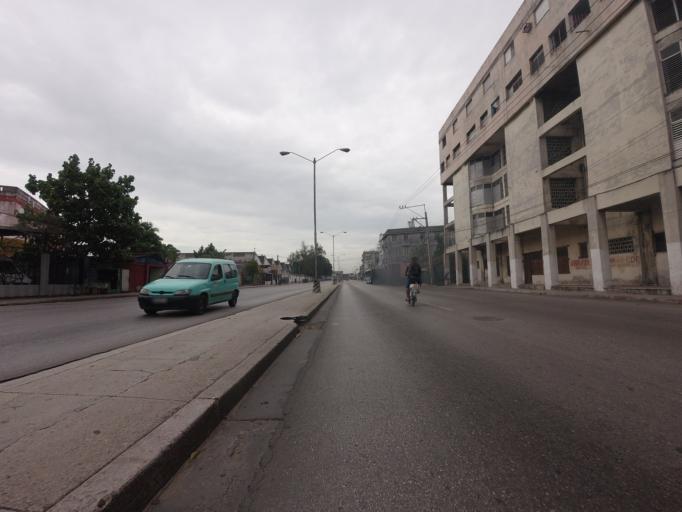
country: CU
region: La Habana
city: La Habana Vieja
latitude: 23.1205
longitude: -82.3652
